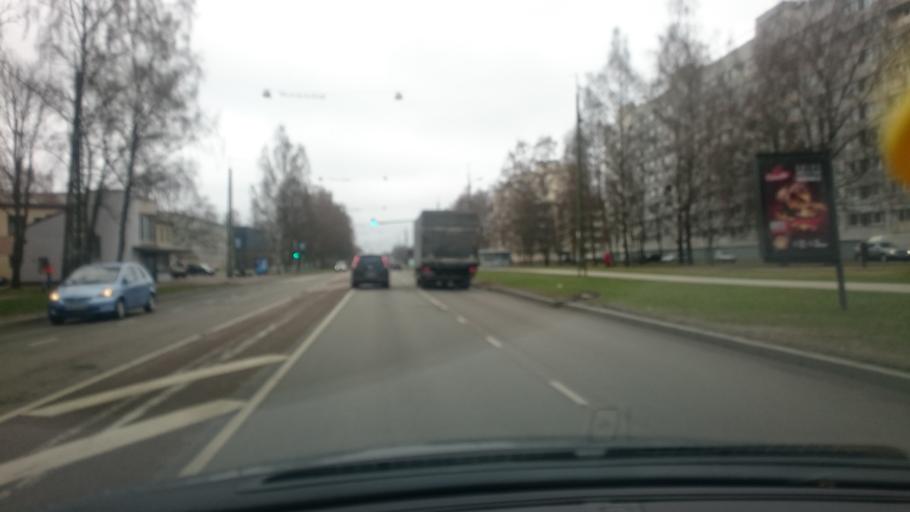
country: EE
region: Harju
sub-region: Tallinna linn
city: Tallinn
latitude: 59.4435
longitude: 24.7037
